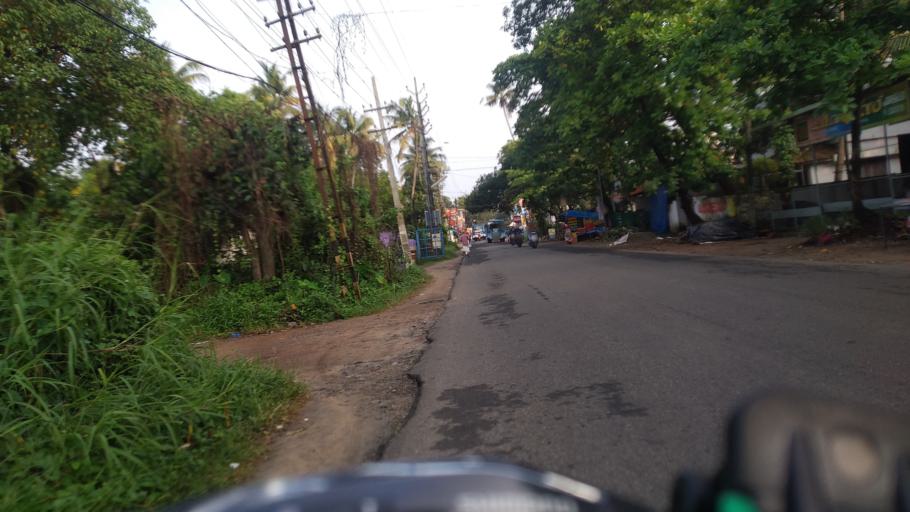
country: IN
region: Kerala
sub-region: Ernakulam
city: Elur
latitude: 10.0395
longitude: 76.2194
